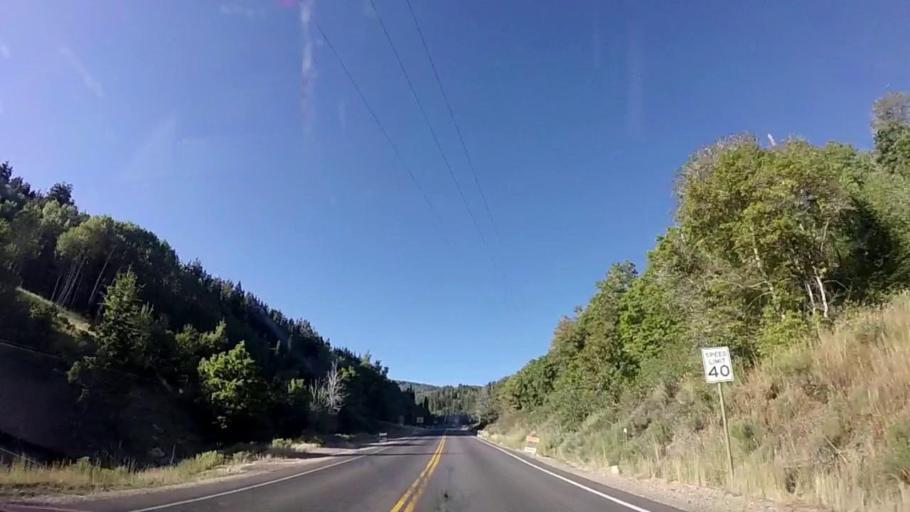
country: US
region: Utah
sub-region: Summit County
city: Park City
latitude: 40.6379
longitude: -111.4932
